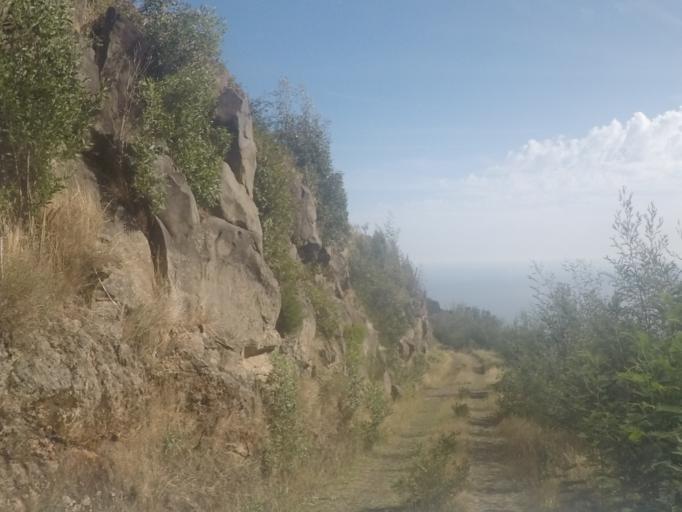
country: PT
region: Madeira
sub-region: Funchal
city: Nossa Senhora do Monte
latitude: 32.6990
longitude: -16.9113
